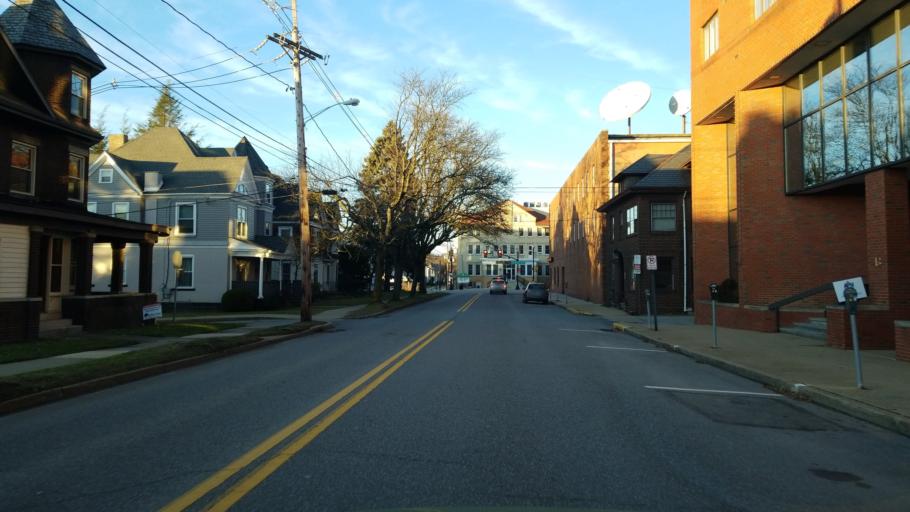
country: US
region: Pennsylvania
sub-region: Indiana County
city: Indiana
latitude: 40.6220
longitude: -79.1559
